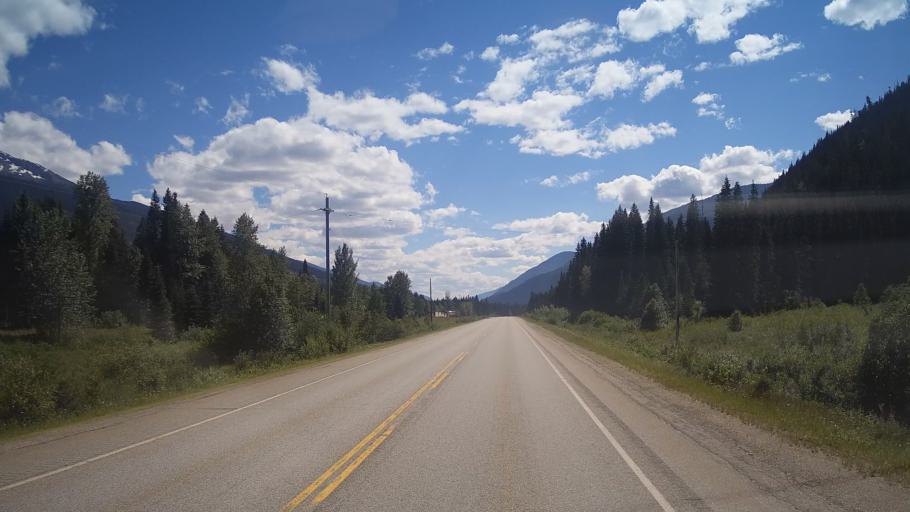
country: CA
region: Alberta
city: Jasper Park Lodge
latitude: 52.5794
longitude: -119.0964
